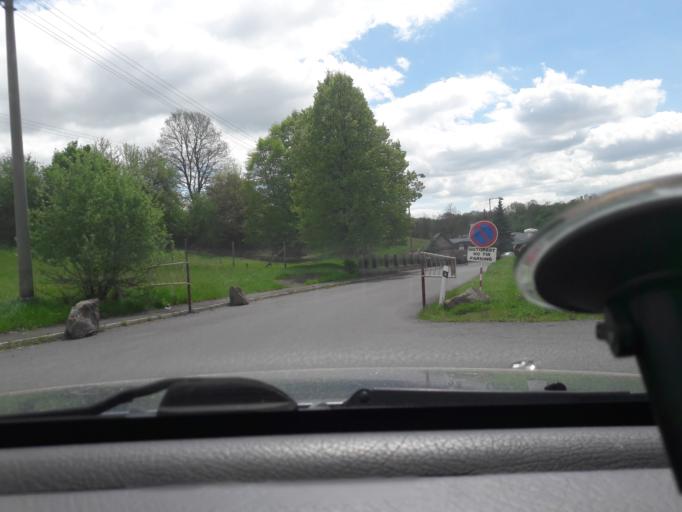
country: SK
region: Banskobystricky
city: Krupina
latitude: 48.3040
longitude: 19.0272
